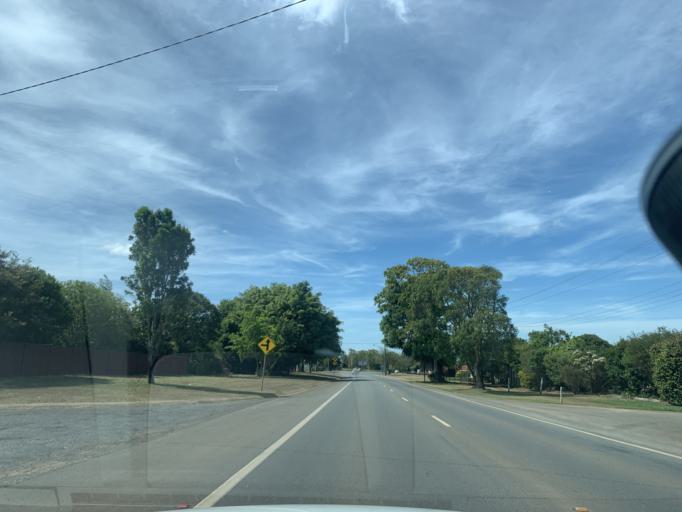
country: AU
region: Queensland
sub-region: Tablelands
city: Tolga
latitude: -17.2215
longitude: 145.4789
